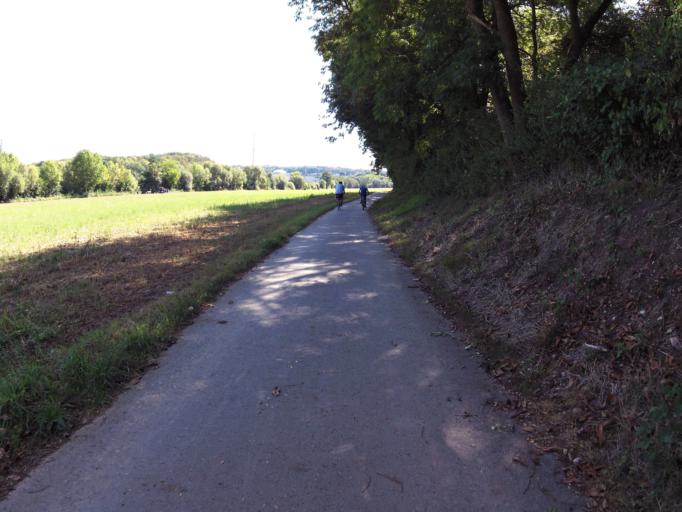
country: DE
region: Baden-Wuerttemberg
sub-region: Regierungsbezirk Stuttgart
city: Neckarwestheim
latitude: 49.0518
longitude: 9.1727
